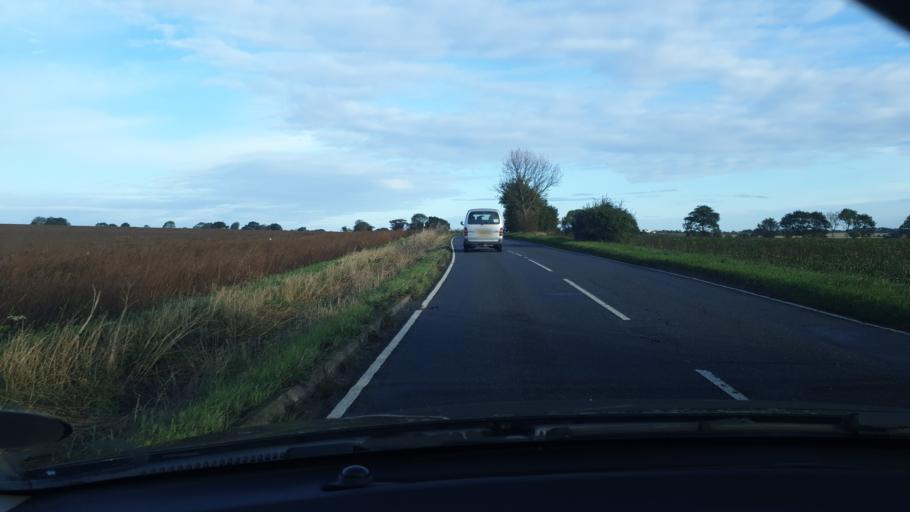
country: GB
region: England
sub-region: Essex
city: Little Clacton
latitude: 51.8724
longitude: 1.1733
